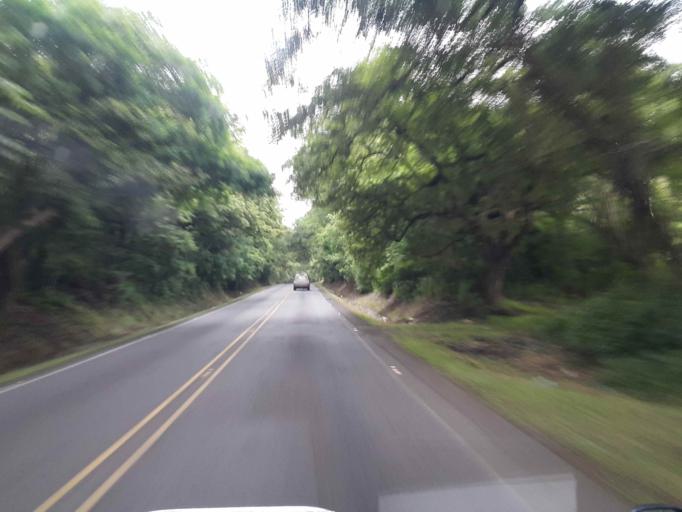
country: CR
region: Puntarenas
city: Miramar
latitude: 10.0818
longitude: -84.7851
